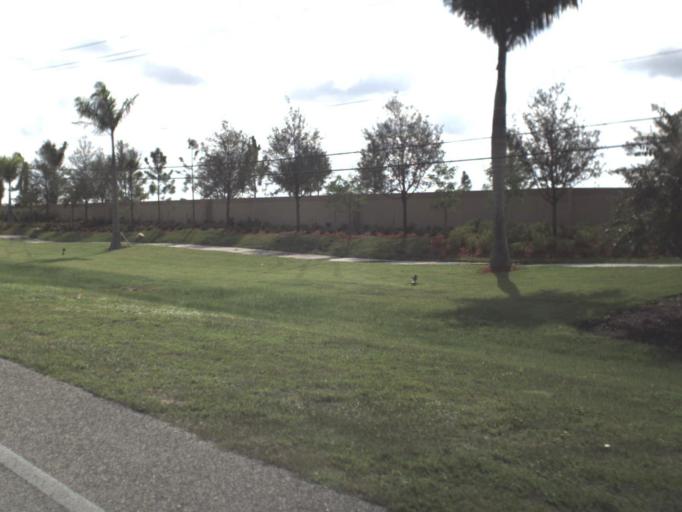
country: US
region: Florida
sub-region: Sarasota County
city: Plantation
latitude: 27.0495
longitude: -82.3514
